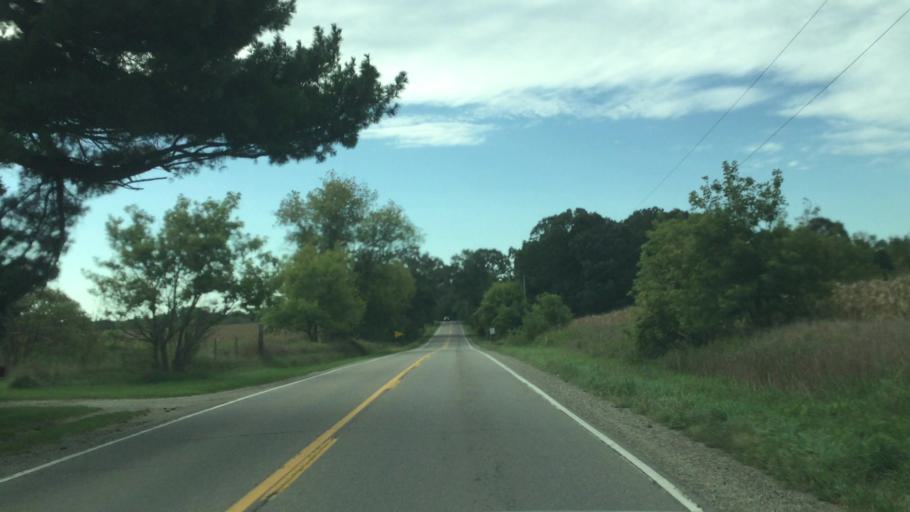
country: US
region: Michigan
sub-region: Genesee County
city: Argentine
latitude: 42.7022
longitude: -83.8405
